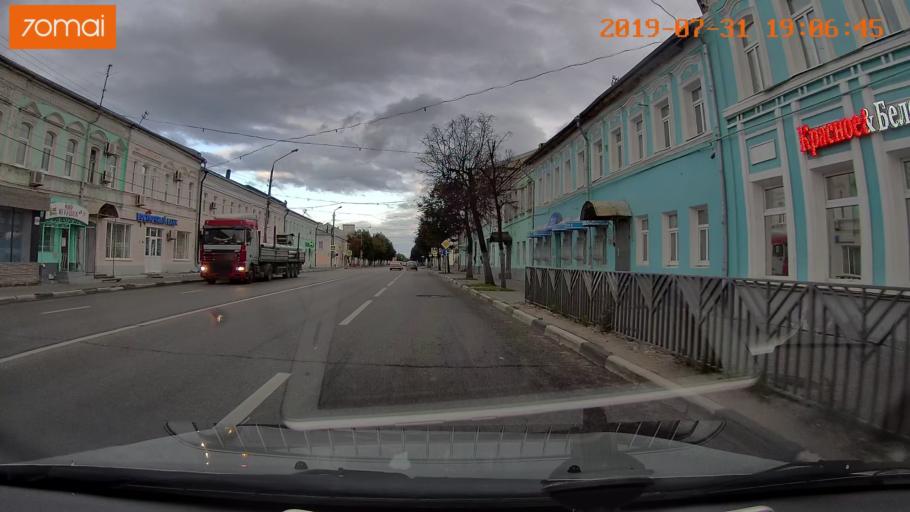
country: RU
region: Moskovskaya
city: Kolomna
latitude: 55.1008
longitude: 38.7561
